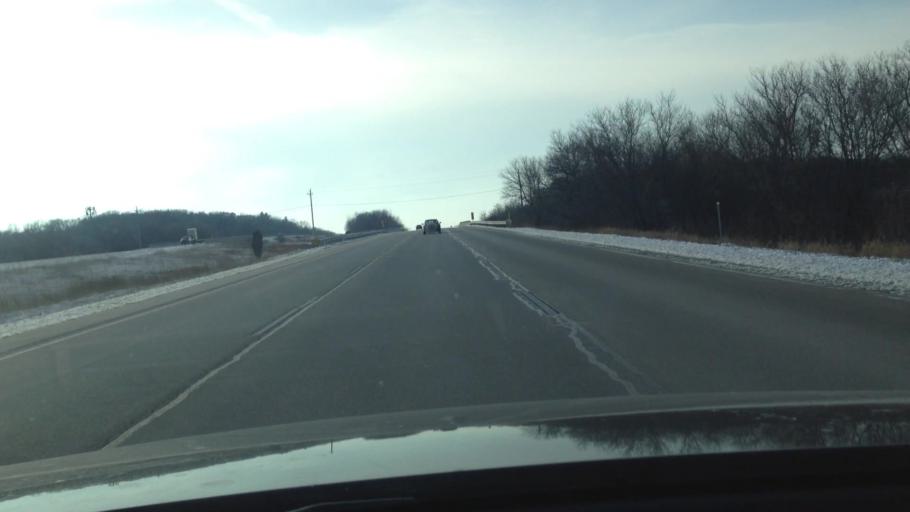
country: US
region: Wisconsin
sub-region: Walworth County
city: East Troy
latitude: 42.7750
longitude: -88.4031
